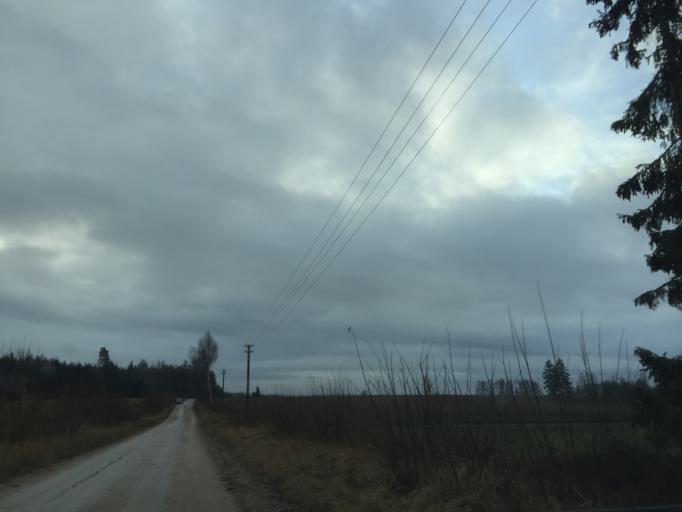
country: LV
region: Vainode
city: Vainode
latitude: 56.6095
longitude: 21.7977
